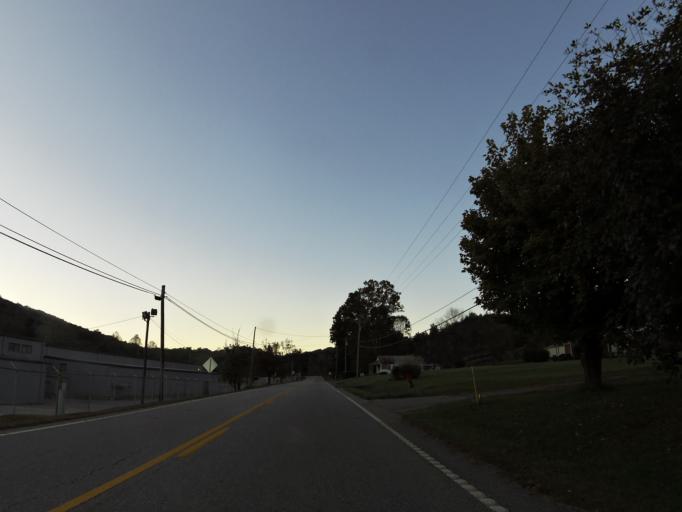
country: US
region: Tennessee
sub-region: Anderson County
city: Rocky Top
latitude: 36.2573
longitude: -84.1832
